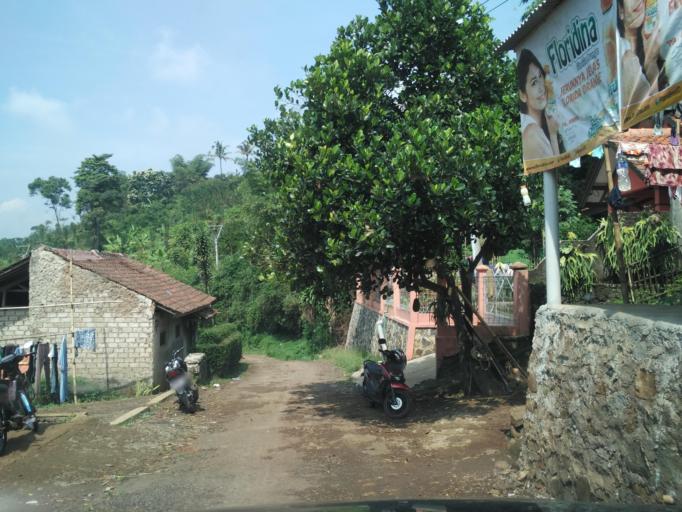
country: ID
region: West Java
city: Ciranjang-hilir
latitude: -6.7904
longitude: 107.1082
